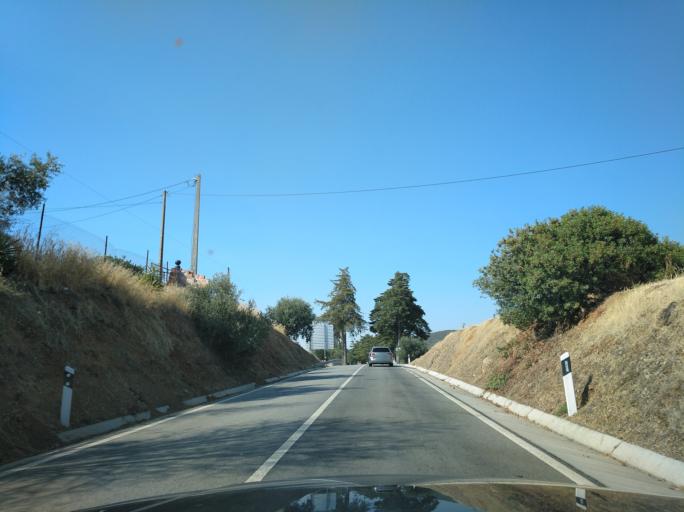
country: ES
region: Andalusia
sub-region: Provincia de Huelva
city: Rosal de la Frontera
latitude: 37.9509
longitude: -7.3025
